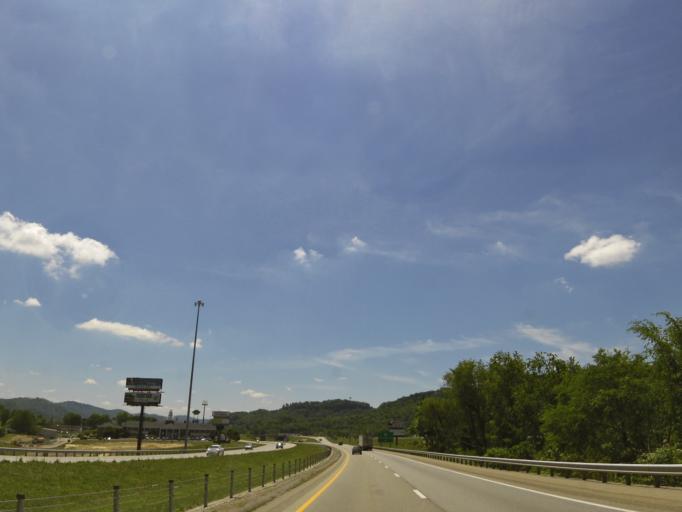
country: US
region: Kentucky
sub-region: Whitley County
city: Williamsburg
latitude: 36.7295
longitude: -84.1707
